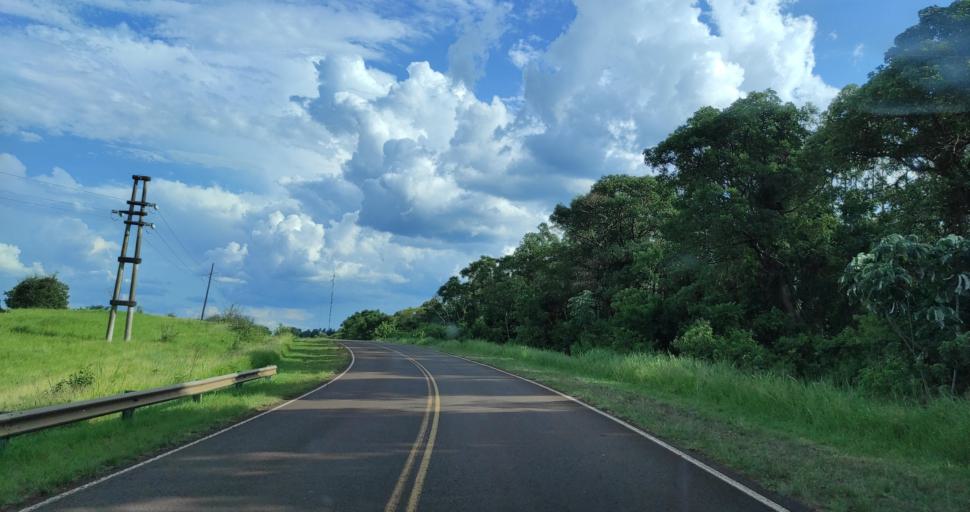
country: AR
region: Misiones
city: San Vicente
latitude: -26.3608
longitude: -54.2160
